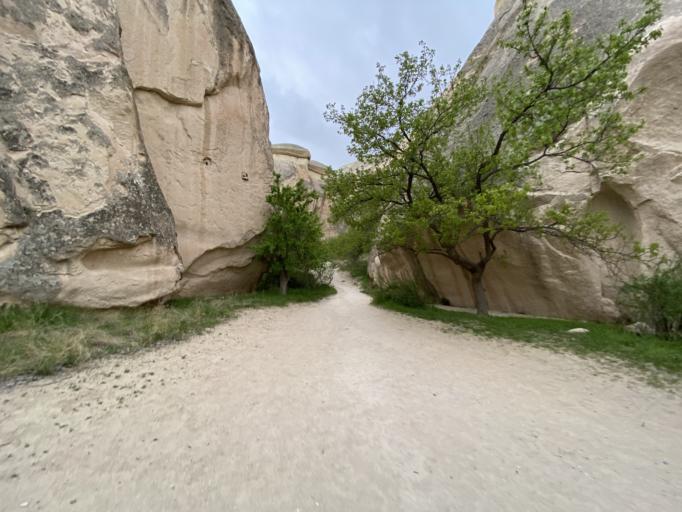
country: TR
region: Nevsehir
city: Goereme
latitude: 38.6763
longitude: 34.8564
